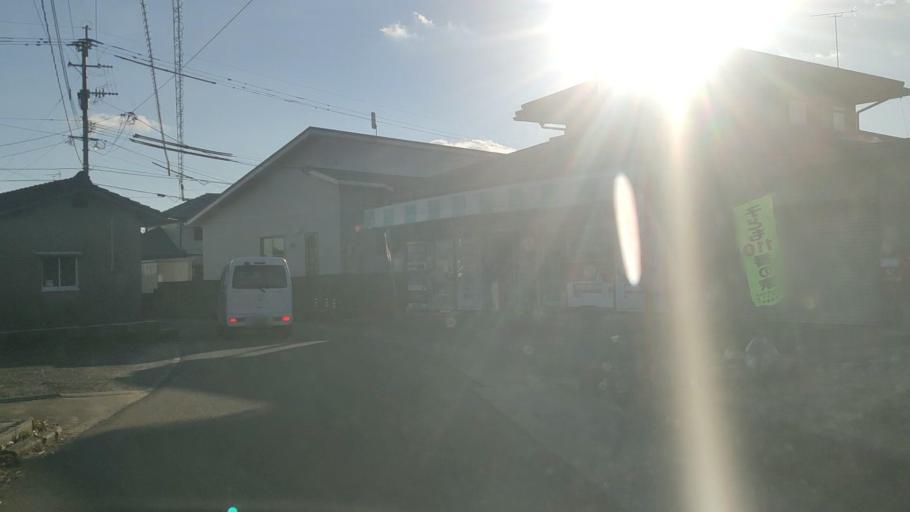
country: JP
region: Saga Prefecture
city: Saga-shi
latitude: 33.2945
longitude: 130.2414
